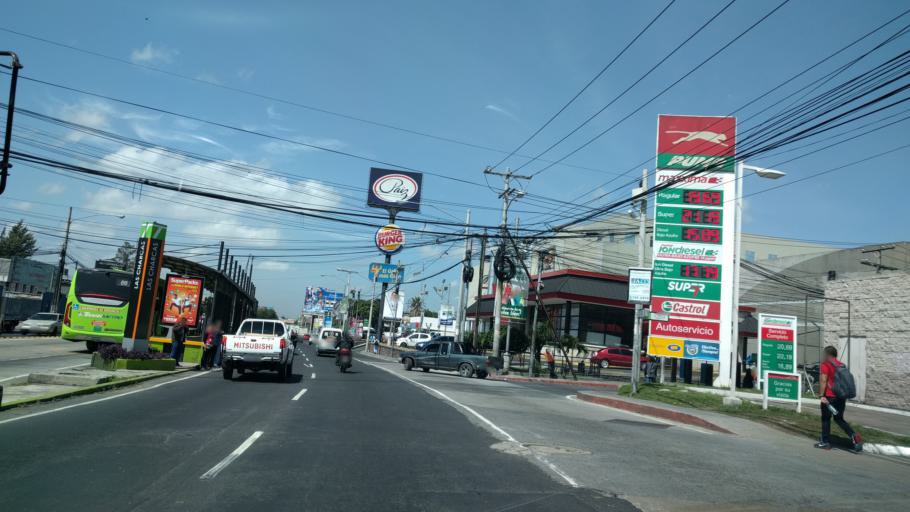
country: GT
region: Guatemala
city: Mixco
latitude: 14.5943
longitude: -90.5580
